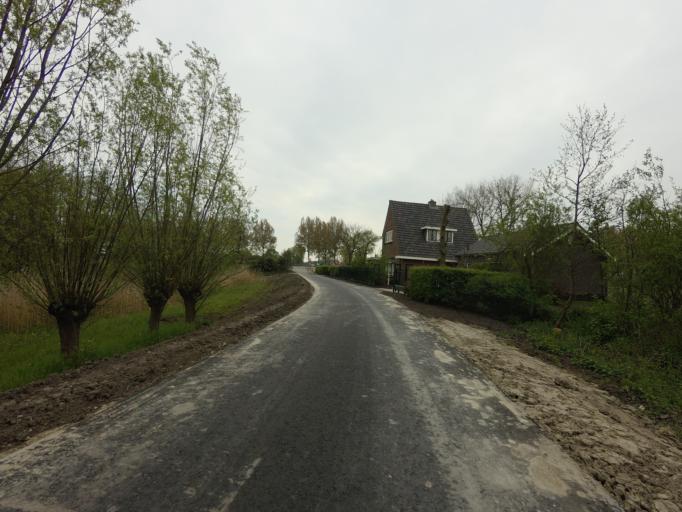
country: NL
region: North Holland
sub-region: Gemeente Diemen
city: Diemen
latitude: 52.3345
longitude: 4.9800
